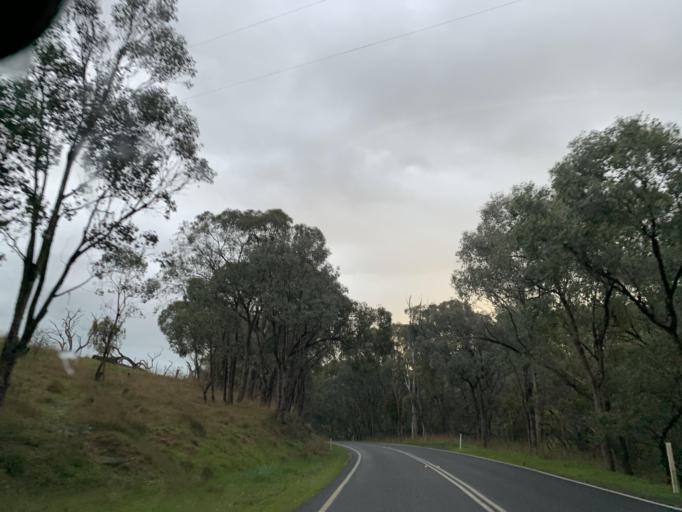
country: AU
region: Victoria
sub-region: Murrindindi
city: Kinglake West
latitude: -37.2205
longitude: 145.1256
